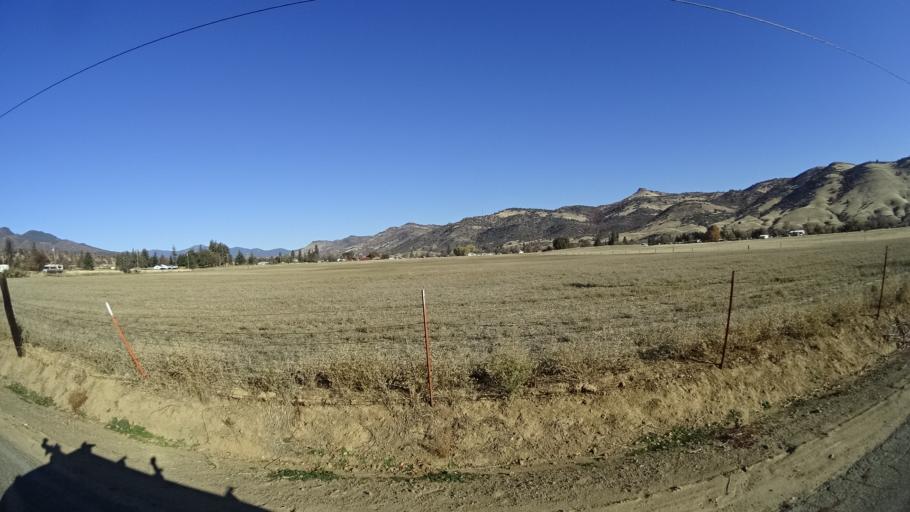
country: US
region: California
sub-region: Siskiyou County
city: Montague
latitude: 41.9024
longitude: -122.5604
